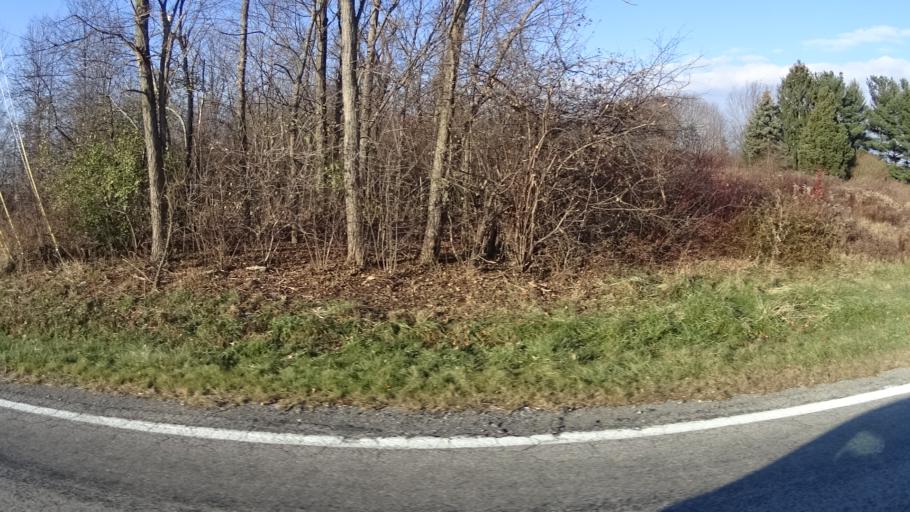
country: US
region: Ohio
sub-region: Lorain County
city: Camden
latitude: 41.2521
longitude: -82.2561
